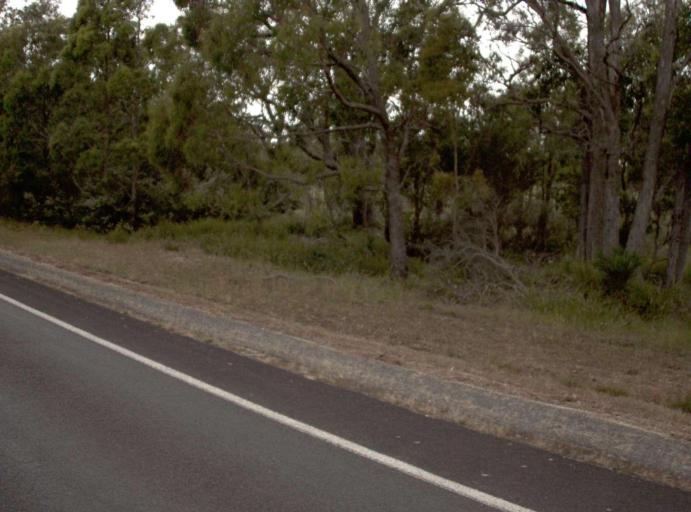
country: AU
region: Victoria
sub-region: Wellington
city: Sale
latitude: -38.4960
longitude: 146.9035
